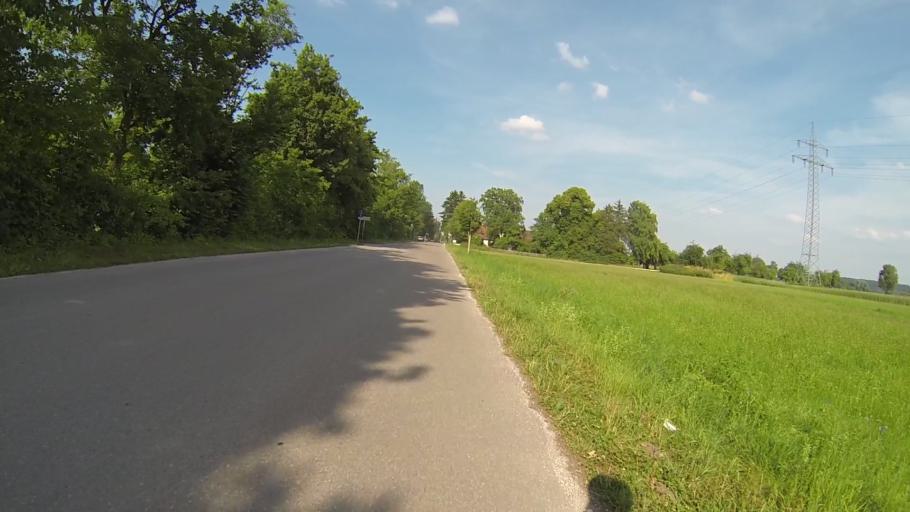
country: DE
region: Bavaria
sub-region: Swabia
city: Neu-Ulm
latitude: 48.3624
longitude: 10.0217
